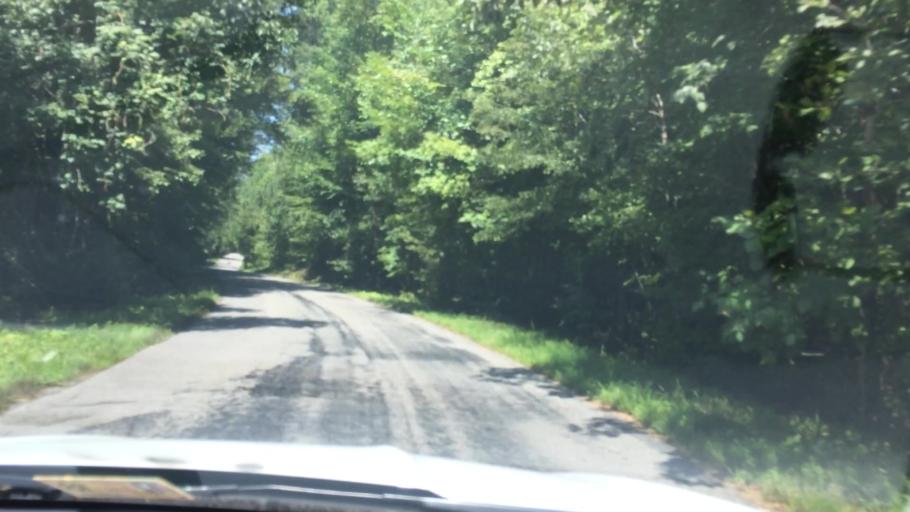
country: US
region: Virginia
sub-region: Charles City County
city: Charles City
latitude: 37.2777
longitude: -76.9285
